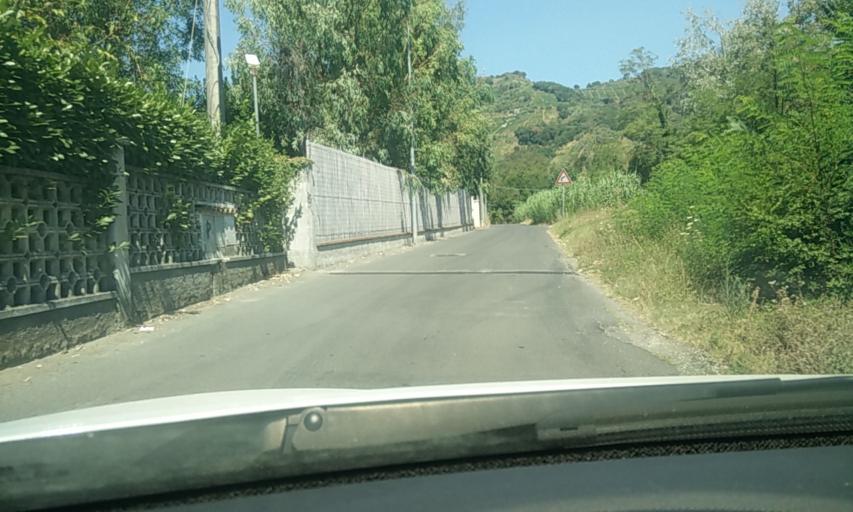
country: IT
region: Tuscany
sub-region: Provincia di Massa-Carrara
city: Massa
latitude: 44.0415
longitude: 10.1031
